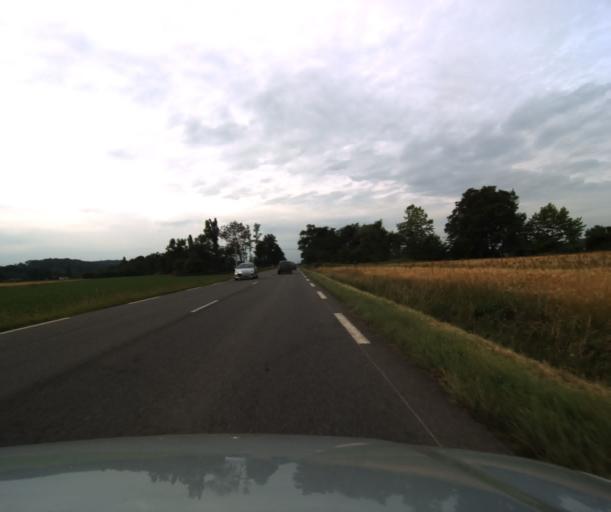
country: FR
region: Midi-Pyrenees
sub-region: Departement des Hautes-Pyrenees
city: Rabastens-de-Bigorre
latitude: 43.3639
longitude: 0.1418
